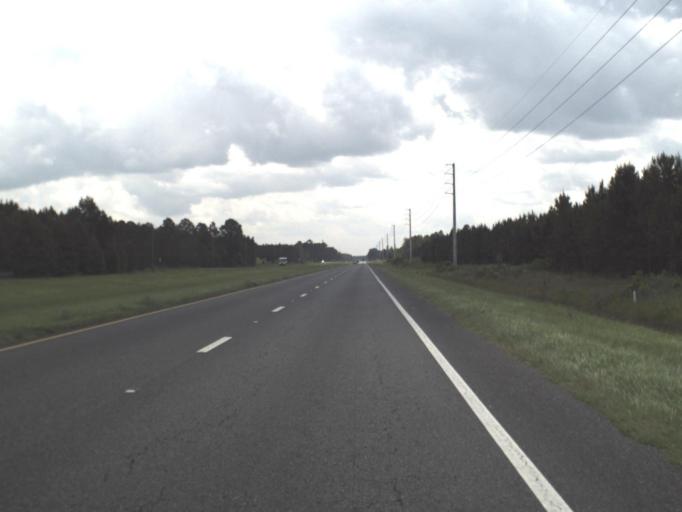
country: US
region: Florida
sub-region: Levy County
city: Bronson
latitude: 29.4721
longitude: -82.6770
